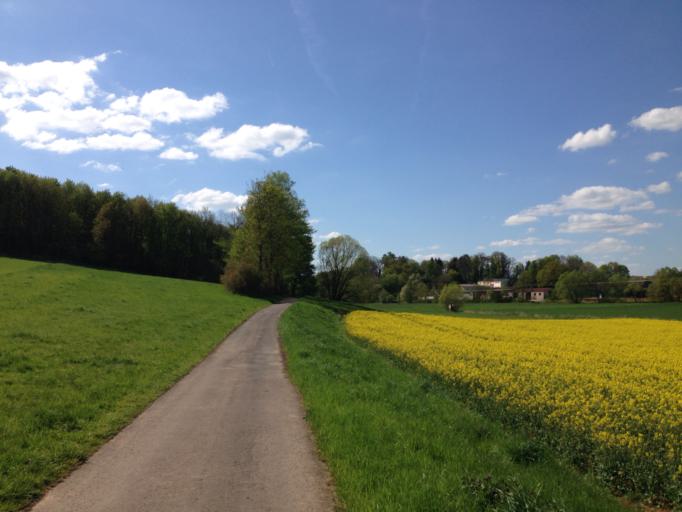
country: DE
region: Hesse
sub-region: Regierungsbezirk Giessen
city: Laubach
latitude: 50.5471
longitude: 8.9409
